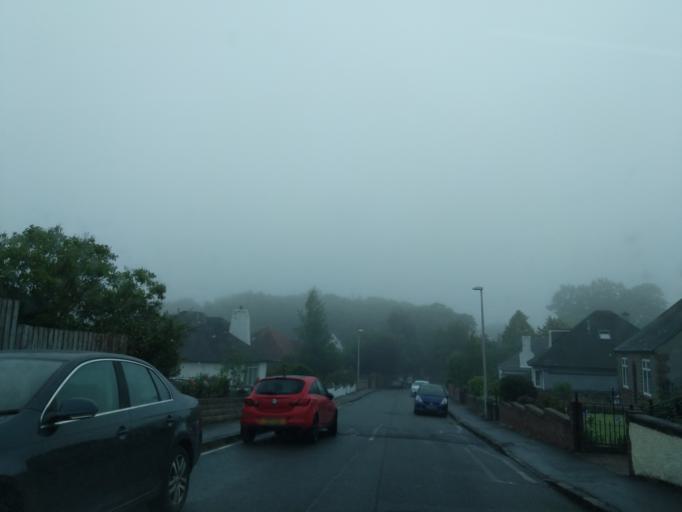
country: GB
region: Scotland
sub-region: West Lothian
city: Seafield
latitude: 55.9435
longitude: -3.1449
